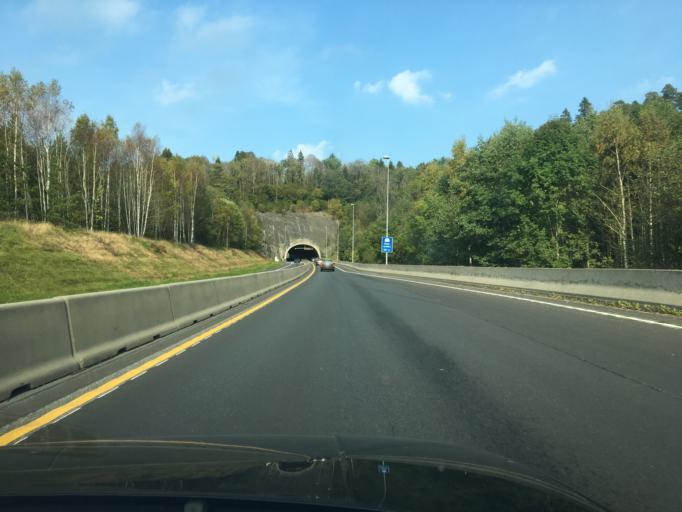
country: NO
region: Telemark
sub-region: Porsgrunn
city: Porsgrunn
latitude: 59.0785
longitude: 9.6647
